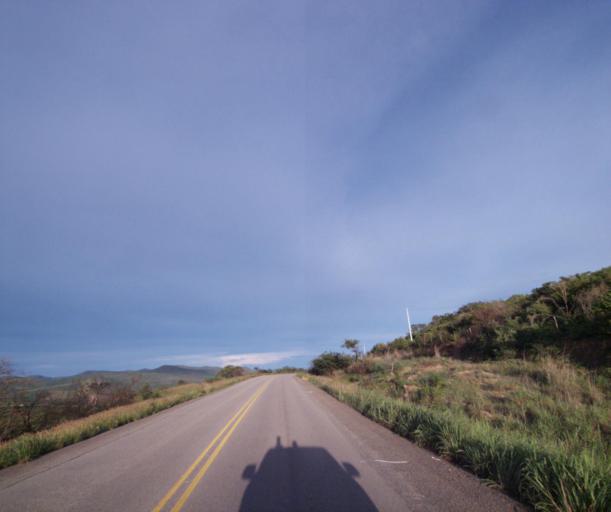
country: BR
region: Bahia
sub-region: Cacule
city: Cacule
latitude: -14.2033
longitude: -42.0602
